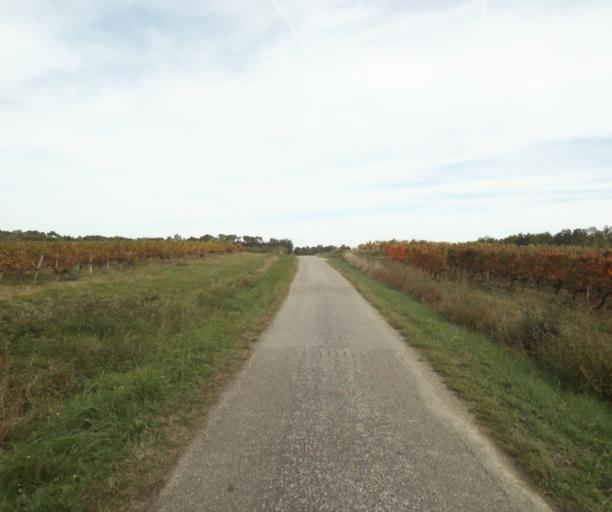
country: FR
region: Midi-Pyrenees
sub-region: Departement du Tarn-et-Garonne
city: Orgueil
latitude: 43.8829
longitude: 1.3916
